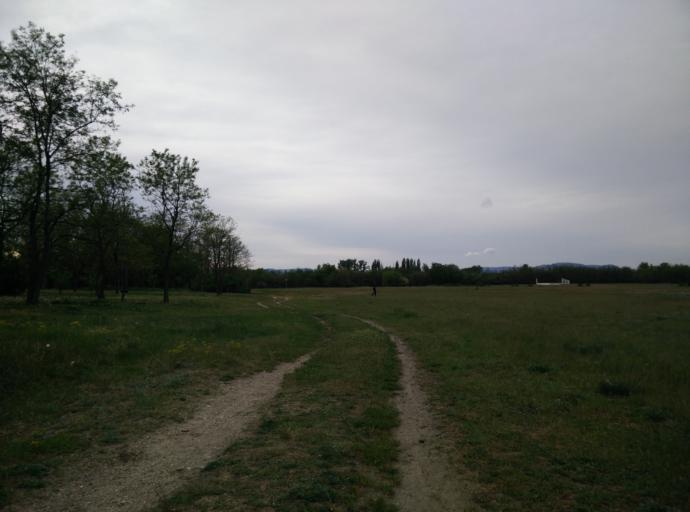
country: HU
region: Pest
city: Dunakeszi
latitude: 47.6114
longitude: 19.1349
